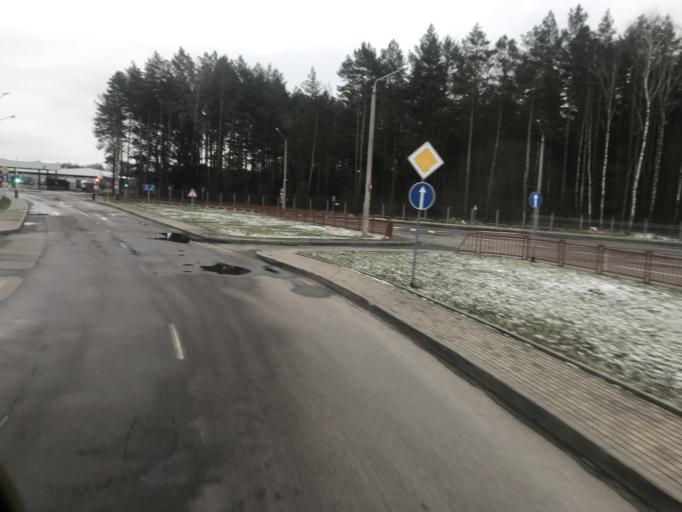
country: BY
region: Grodnenskaya
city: Vyalikaya Byerastavitsa
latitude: 53.1209
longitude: 23.8986
